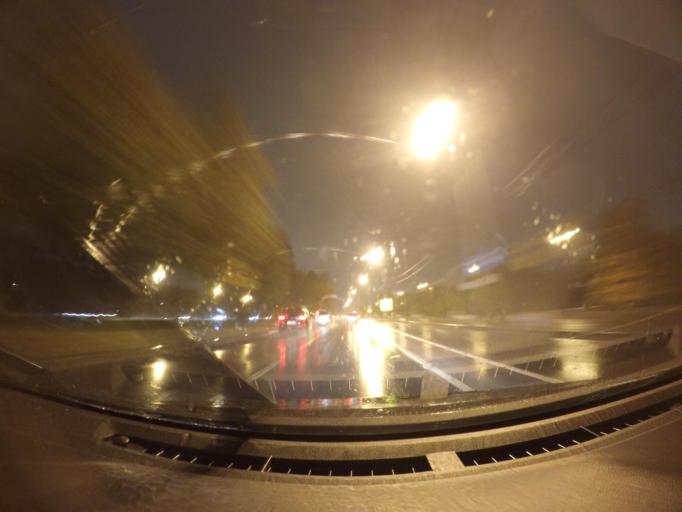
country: RU
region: Moscow
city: Kolomenskoye
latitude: 55.6638
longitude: 37.6579
